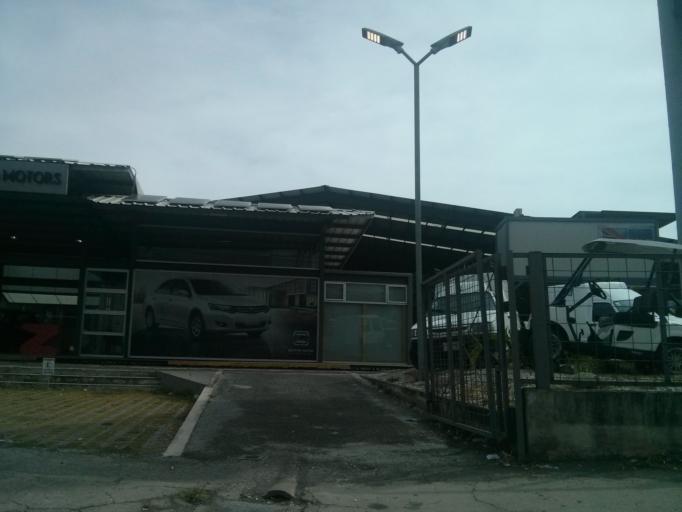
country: CR
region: San Jose
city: Colima
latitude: 9.9482
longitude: -84.0936
